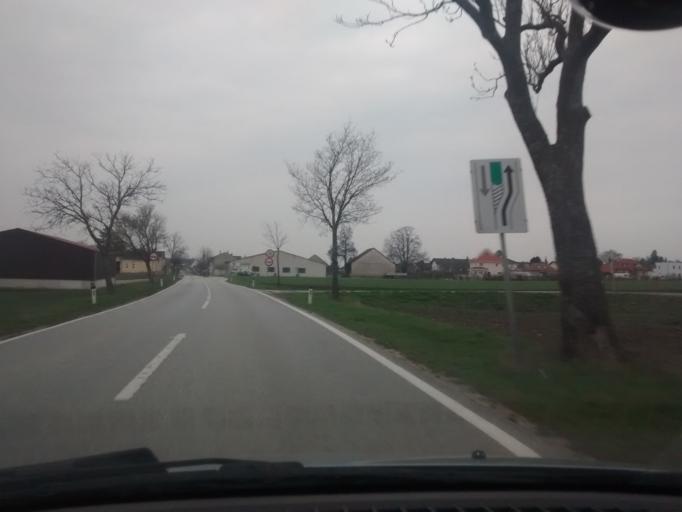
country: AT
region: Lower Austria
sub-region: Politischer Bezirk Wien-Umgebung
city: Gramatneusiedl
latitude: 48.0239
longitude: 16.4697
